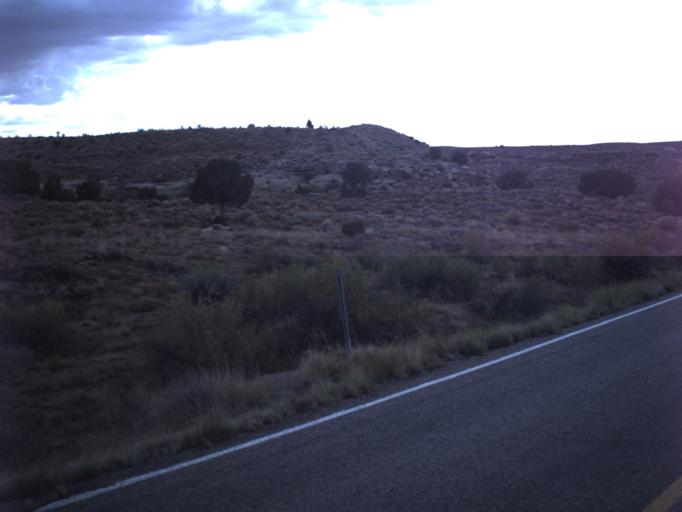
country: US
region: Utah
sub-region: San Juan County
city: Blanding
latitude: 37.4199
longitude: -109.4379
